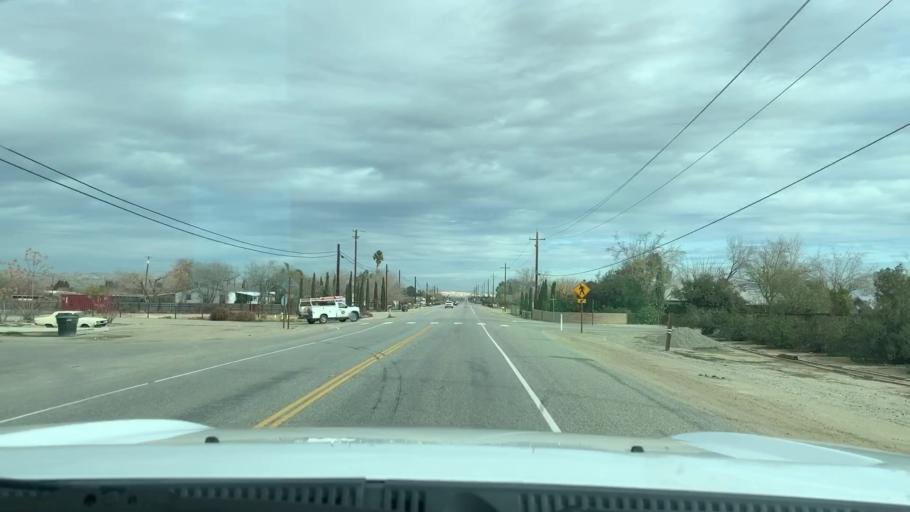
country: US
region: California
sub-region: Kern County
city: Ford City
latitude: 35.2071
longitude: -119.4088
